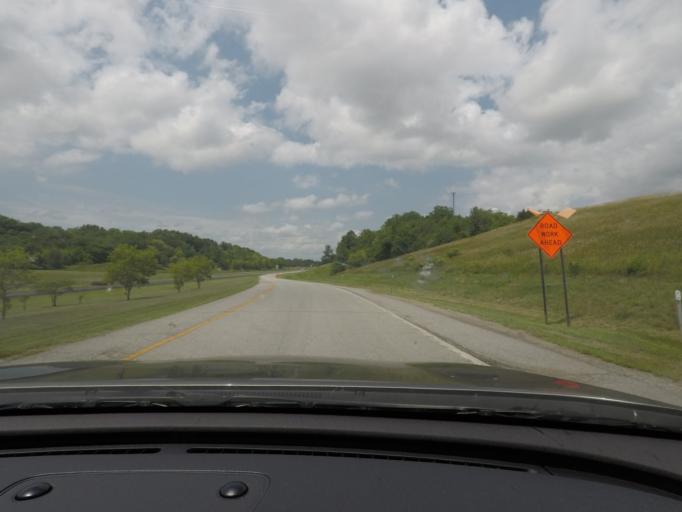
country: US
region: Missouri
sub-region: Carroll County
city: Carrollton
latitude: 39.3598
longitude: -93.4809
